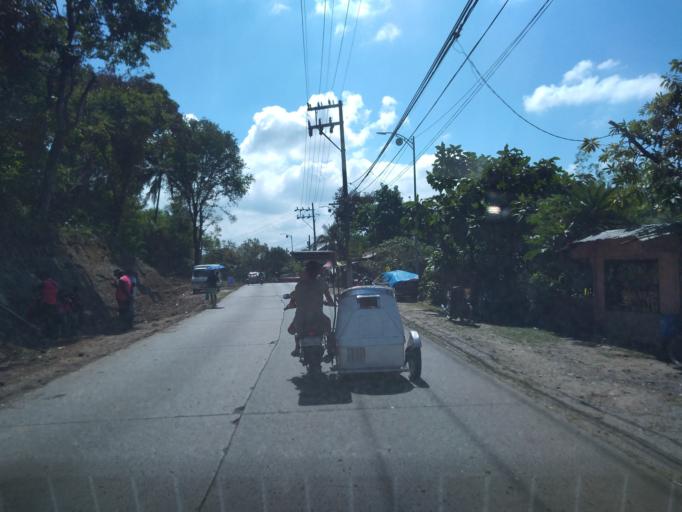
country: PH
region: Central Luzon
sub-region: Province of Bulacan
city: Bitungol
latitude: 14.8598
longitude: 121.0701
